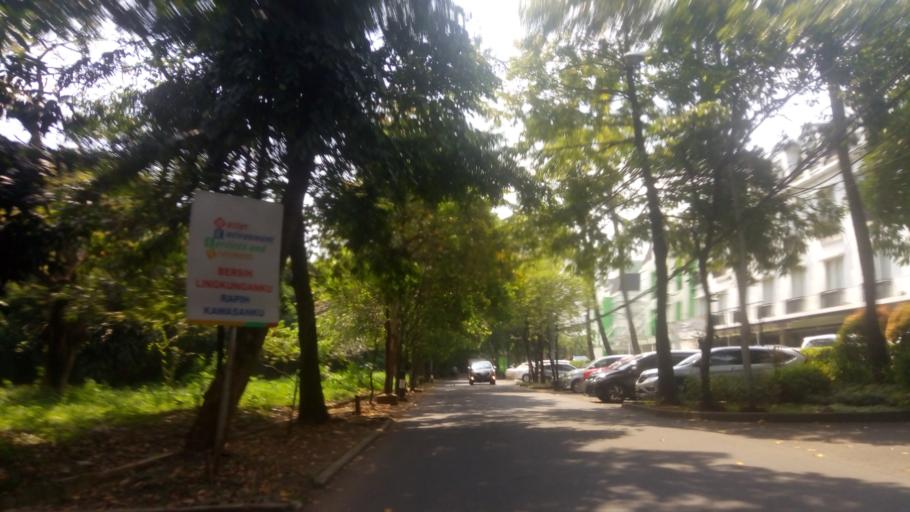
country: ID
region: Jakarta Raya
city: Jakarta
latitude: -6.2389
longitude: 106.8352
